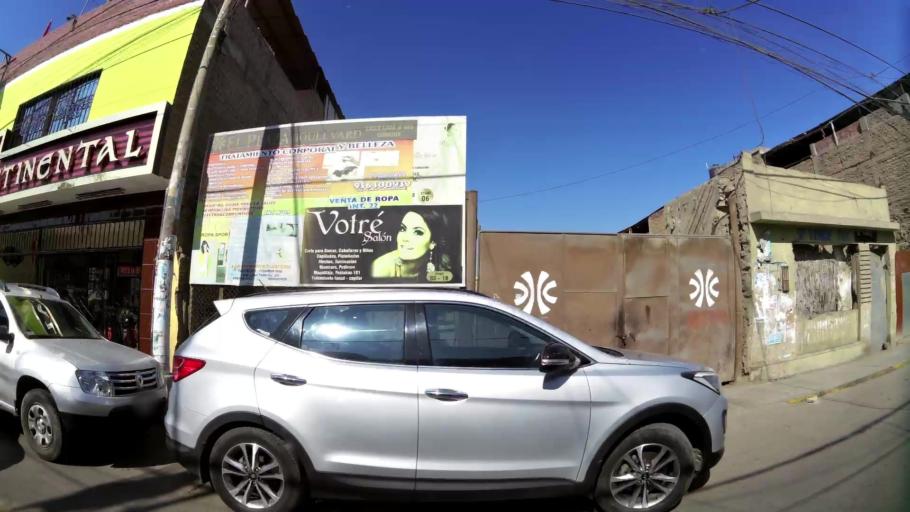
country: PE
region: Ica
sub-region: Provincia de Chincha
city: Chincha Alta
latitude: -13.4208
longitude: -76.1340
